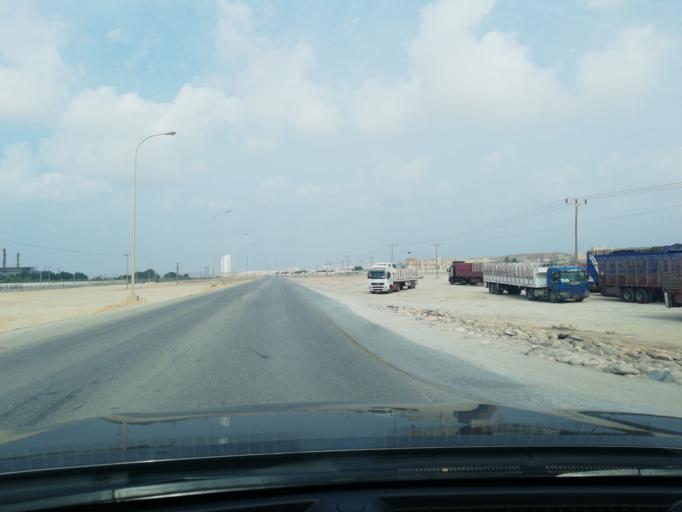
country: OM
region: Zufar
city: Salalah
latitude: 16.9493
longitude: 53.9778
